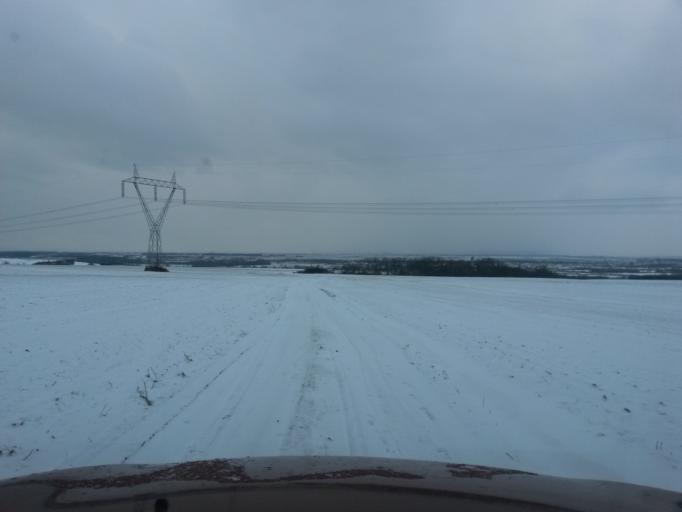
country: SK
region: Kosicky
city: Kosice
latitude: 48.6009
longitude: 21.3714
